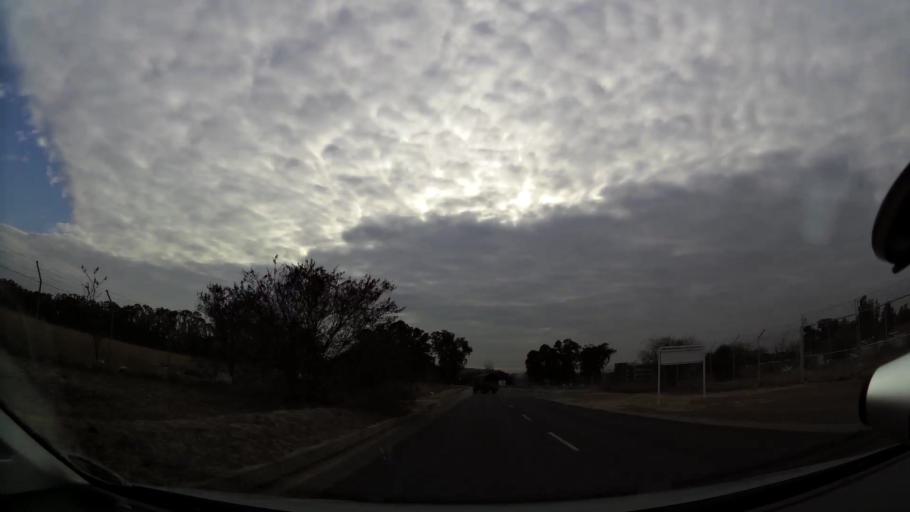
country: ZA
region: Orange Free State
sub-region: Mangaung Metropolitan Municipality
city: Bloemfontein
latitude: -29.1038
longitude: 26.1833
